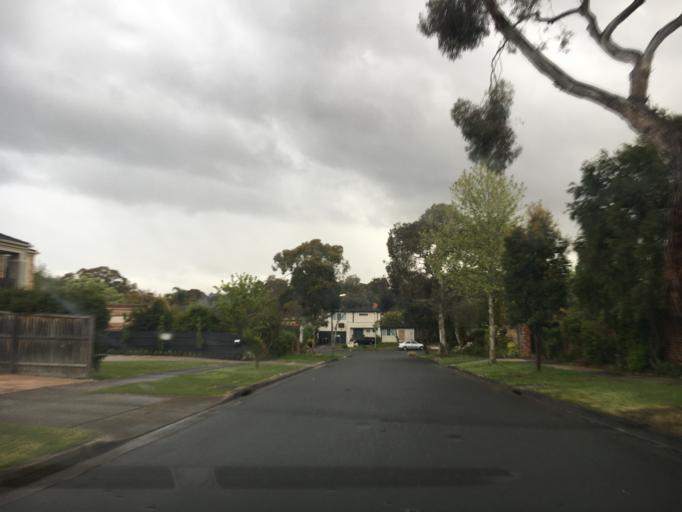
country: AU
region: Victoria
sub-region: Whitehorse
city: Vermont South
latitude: -37.8853
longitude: 145.1860
